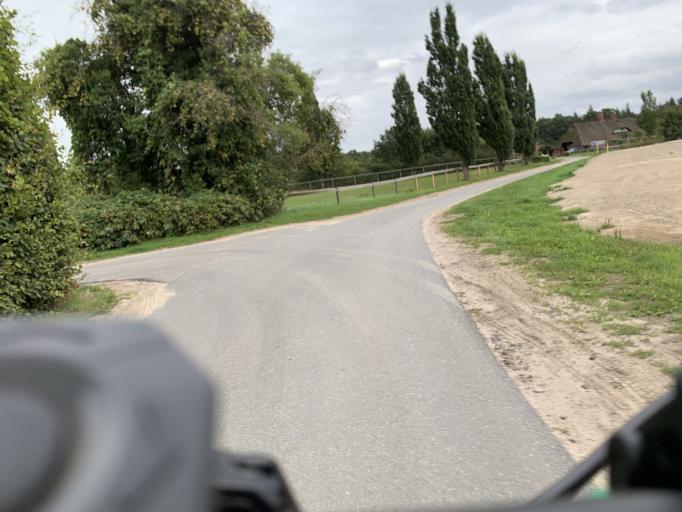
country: DE
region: Lower Saxony
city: Westerstede
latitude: 53.2404
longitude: 7.9264
